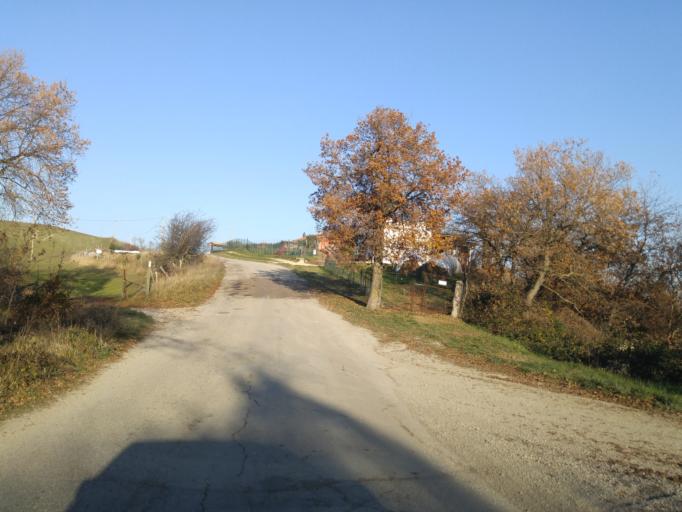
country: IT
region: The Marches
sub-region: Provincia di Pesaro e Urbino
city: Mombaroccio
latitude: 43.7761
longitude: 12.8339
